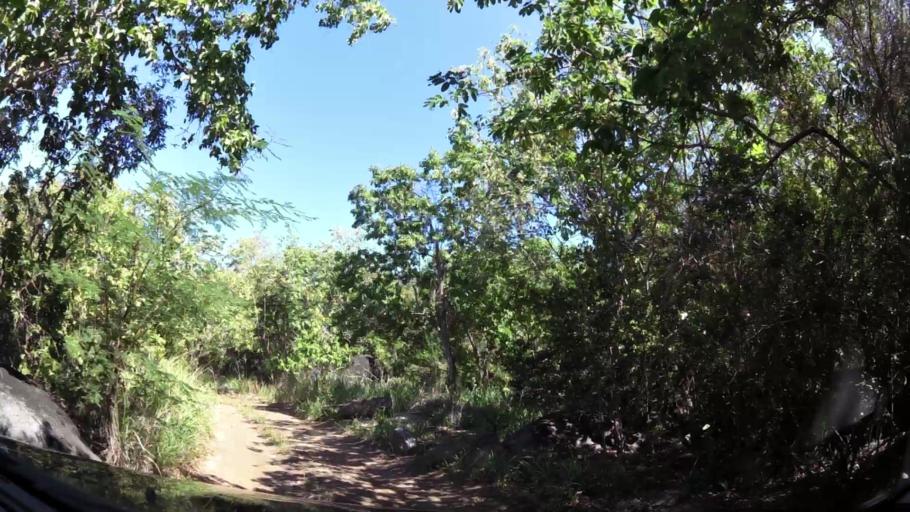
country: VG
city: Tortola
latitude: 18.4438
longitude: -64.5327
